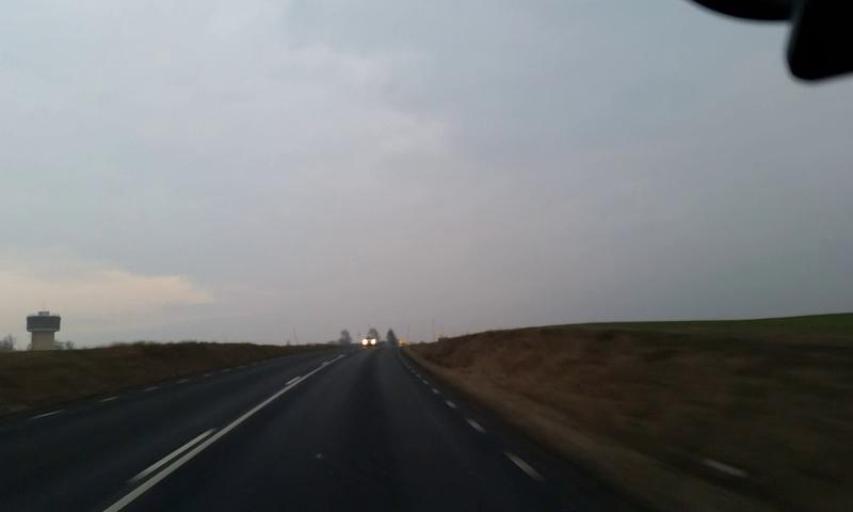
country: SE
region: Skane
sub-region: Angelholms Kommun
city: AEngelholm
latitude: 56.2634
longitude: 12.8879
